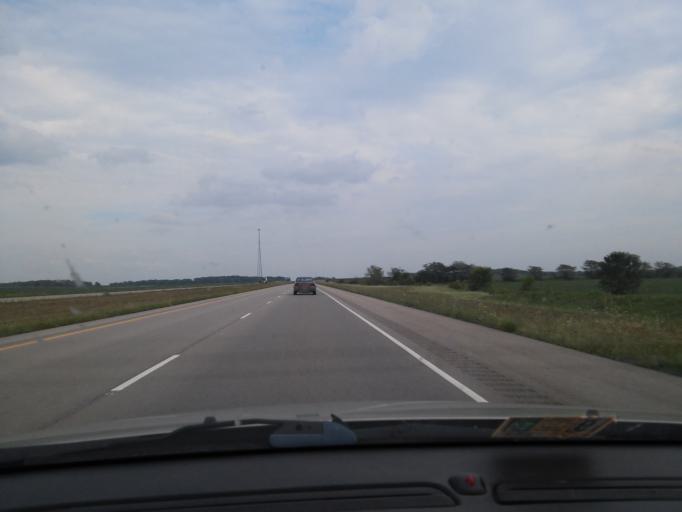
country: US
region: Ohio
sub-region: Ross County
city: Frankfort
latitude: 39.4786
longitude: -83.2818
